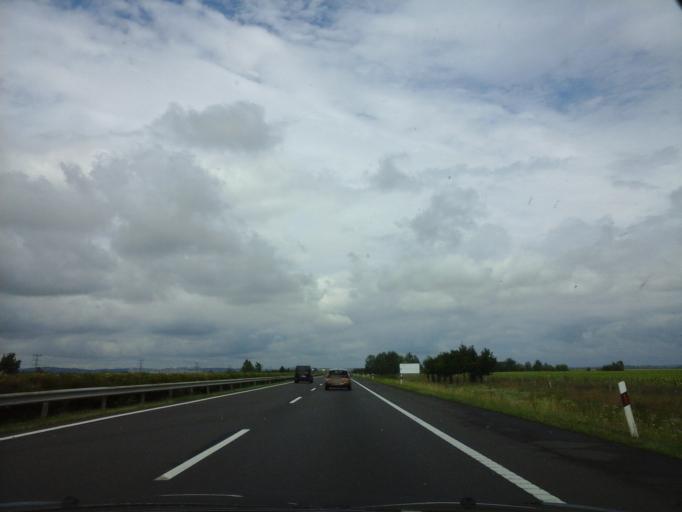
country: HU
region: Borsod-Abauj-Zemplen
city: Malyi
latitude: 48.0188
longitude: 20.8722
